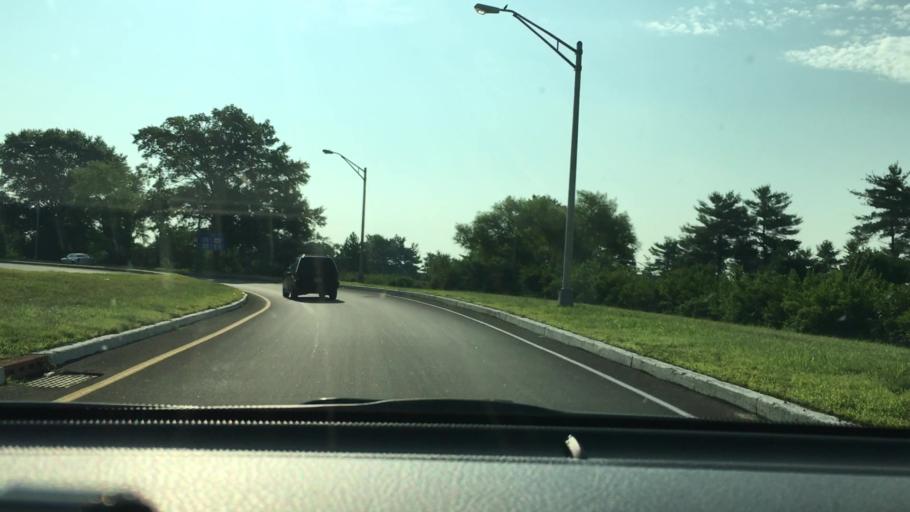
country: US
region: New Jersey
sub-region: Burlington County
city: Mount Laurel
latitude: 39.9657
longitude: -74.9115
